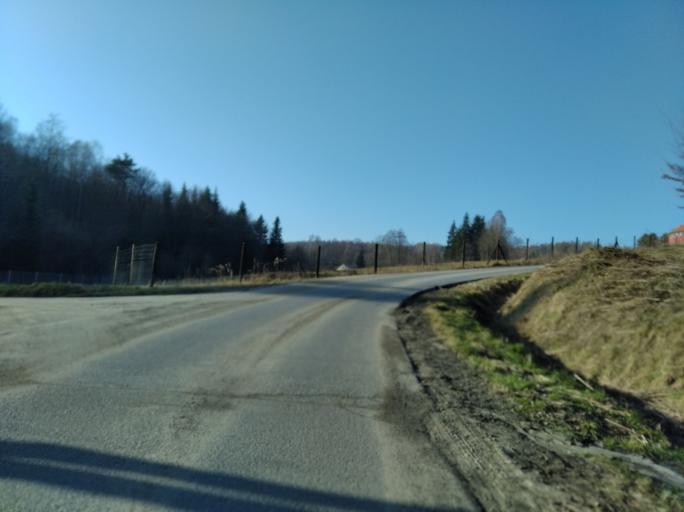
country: PL
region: Subcarpathian Voivodeship
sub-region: Powiat strzyzowski
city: Jawornik
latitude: 49.8259
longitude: 21.8728
